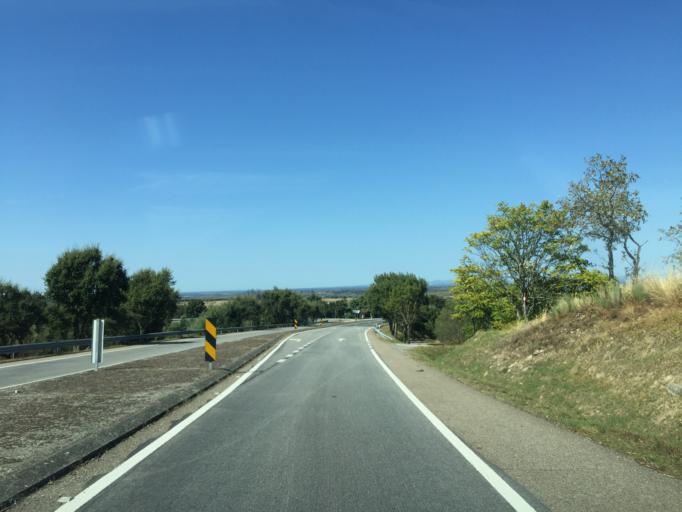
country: PT
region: Portalegre
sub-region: Castelo de Vide
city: Castelo de Vide
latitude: 39.4253
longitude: -7.4797
